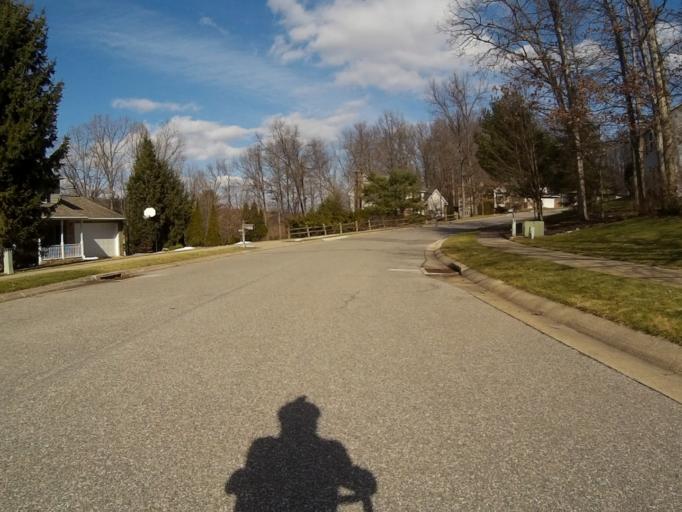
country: US
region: Pennsylvania
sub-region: Centre County
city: Park Forest Village
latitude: 40.8030
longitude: -77.9194
